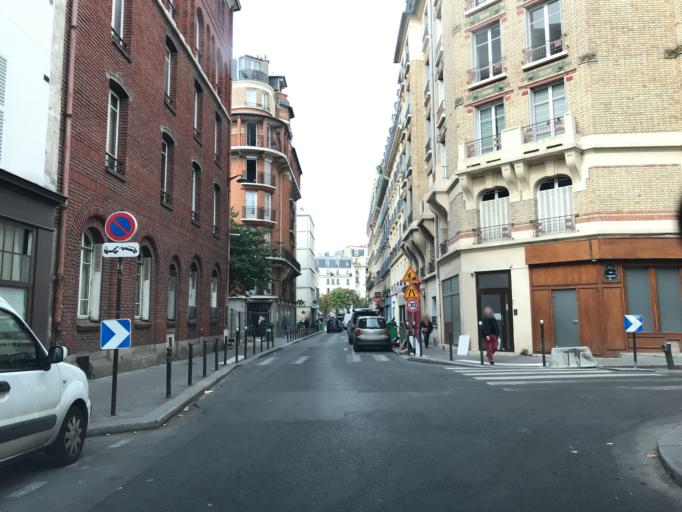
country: FR
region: Ile-de-France
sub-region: Departement des Hauts-de-Seine
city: Malakoff
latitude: 48.8404
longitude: 2.3128
